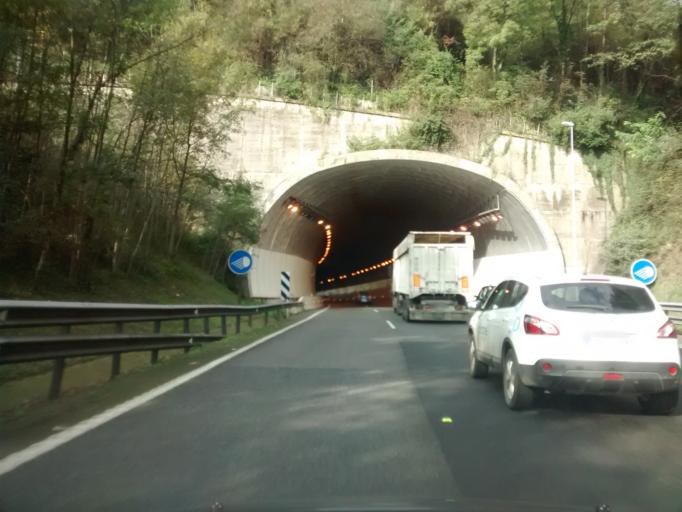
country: ES
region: Basque Country
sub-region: Provincia de Guipuzcoa
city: San Sebastian
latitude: 43.2977
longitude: -1.9891
